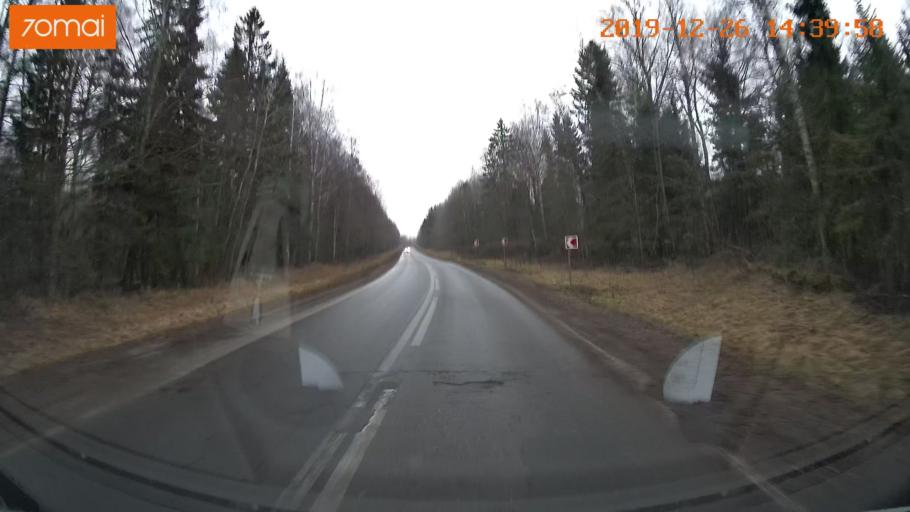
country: RU
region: Jaroslavl
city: Poshekhon'ye
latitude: 58.3788
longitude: 38.9888
